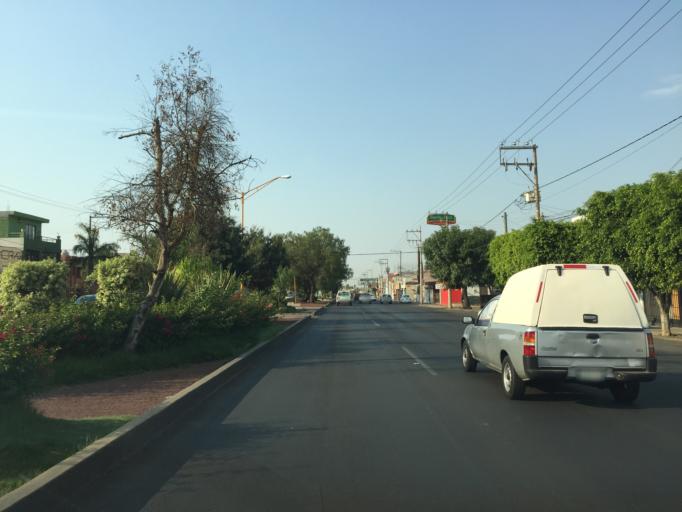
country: MX
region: Aguascalientes
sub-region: Aguascalientes
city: Pocitos
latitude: 21.8941
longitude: -102.3171
